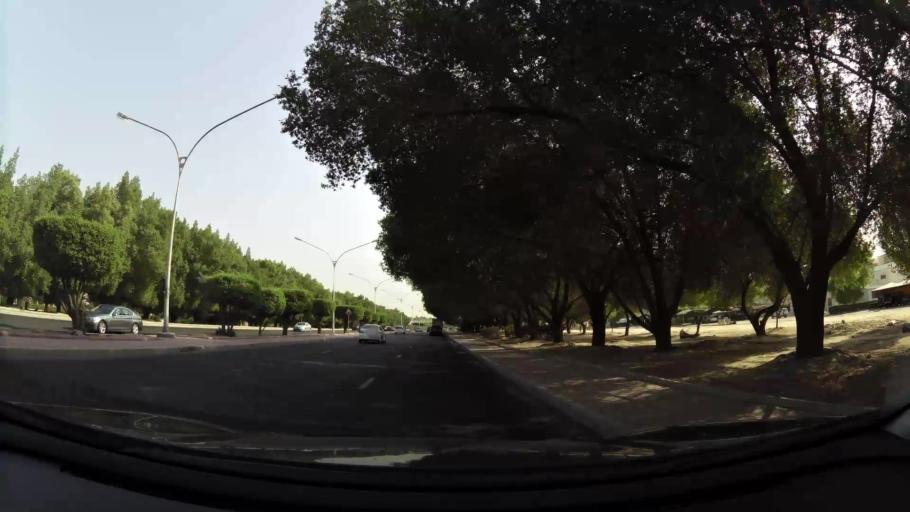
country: KW
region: Muhafazat Hawalli
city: Salwa
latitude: 29.2836
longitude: 48.0606
